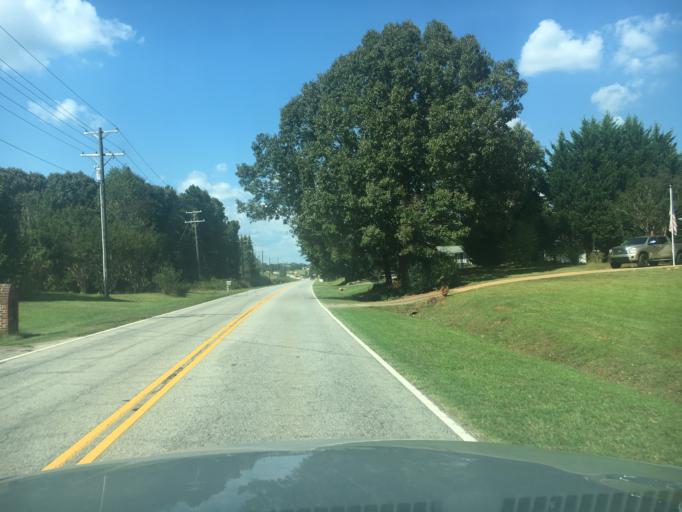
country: US
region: South Carolina
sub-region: Anderson County
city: Pendleton
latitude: 34.5631
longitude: -82.8075
